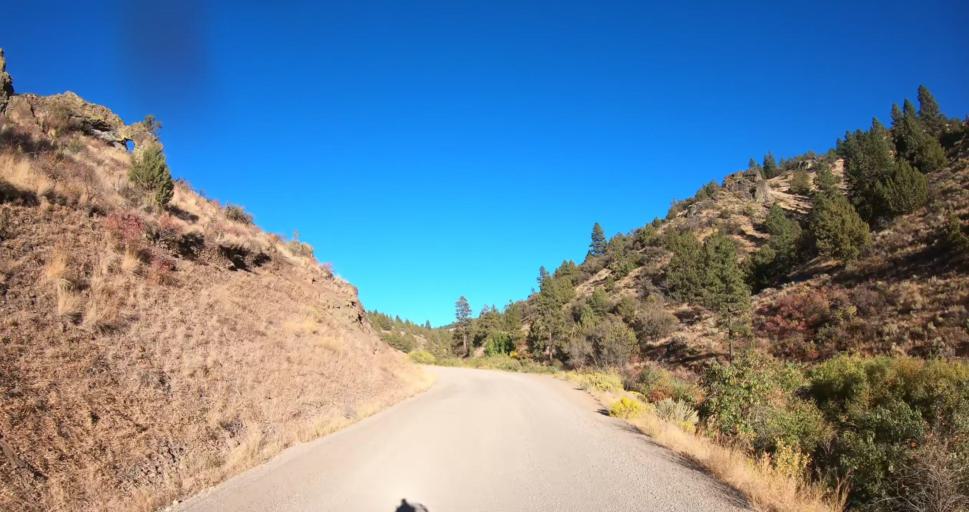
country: US
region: Oregon
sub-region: Lake County
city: Lakeview
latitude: 42.1919
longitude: -120.3307
